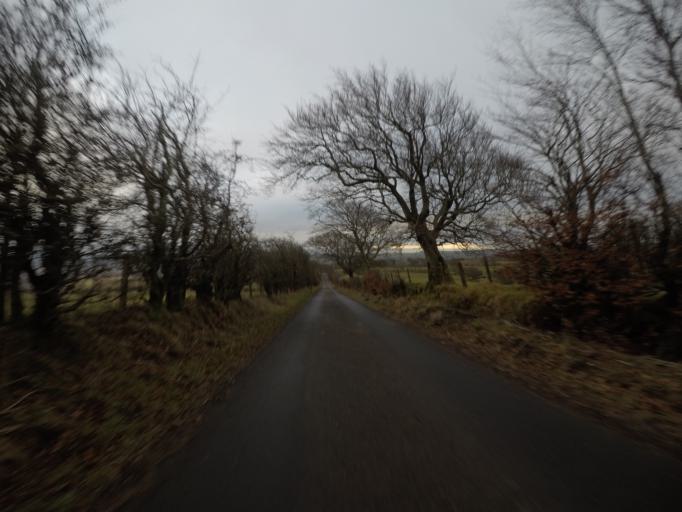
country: GB
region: Scotland
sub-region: North Ayrshire
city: Dalry
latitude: 55.7256
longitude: -4.7637
